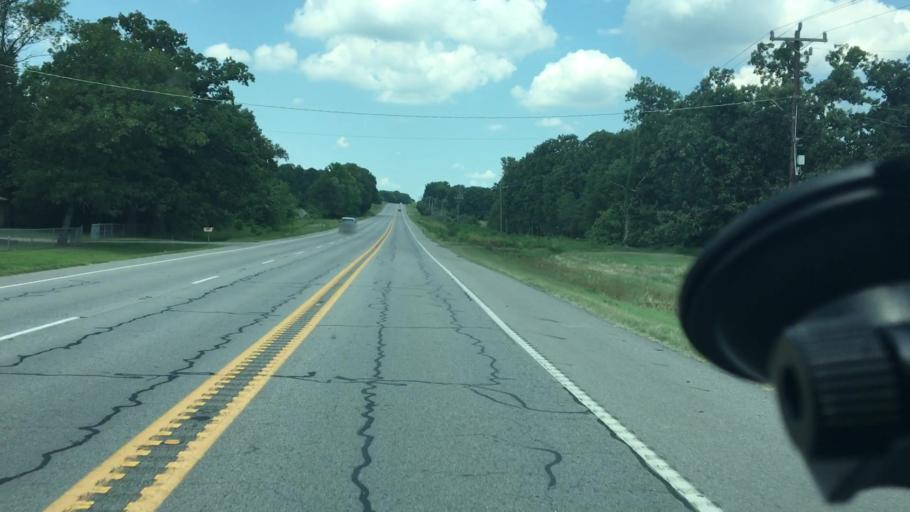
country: US
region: Arkansas
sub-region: Logan County
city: Paris
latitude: 35.2998
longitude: -93.8323
